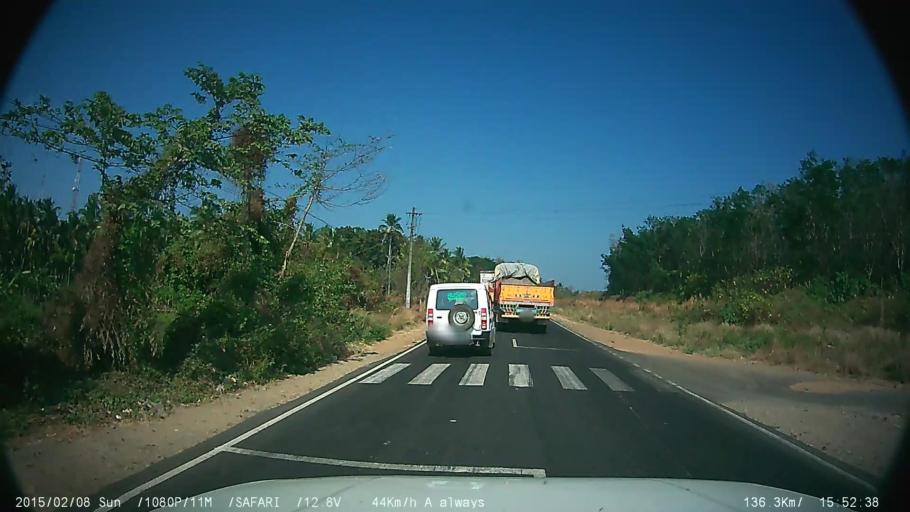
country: IN
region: Kerala
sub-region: Thrissur District
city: Chelakara
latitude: 10.5834
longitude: 76.4314
